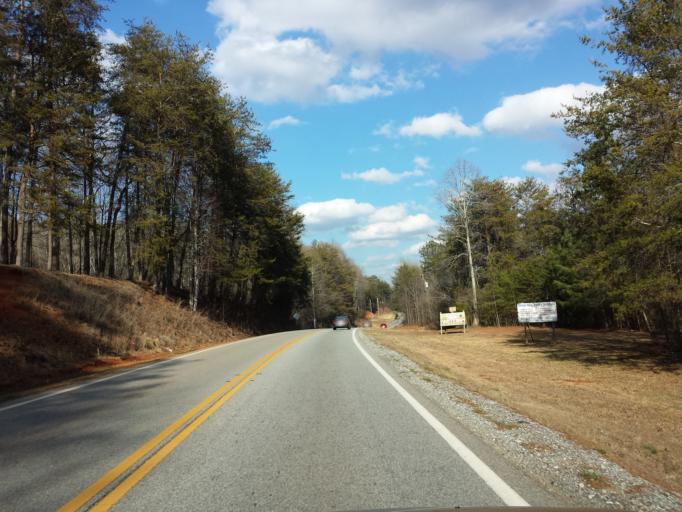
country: US
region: Georgia
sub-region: Lumpkin County
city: Dahlonega
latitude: 34.5004
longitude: -83.9376
